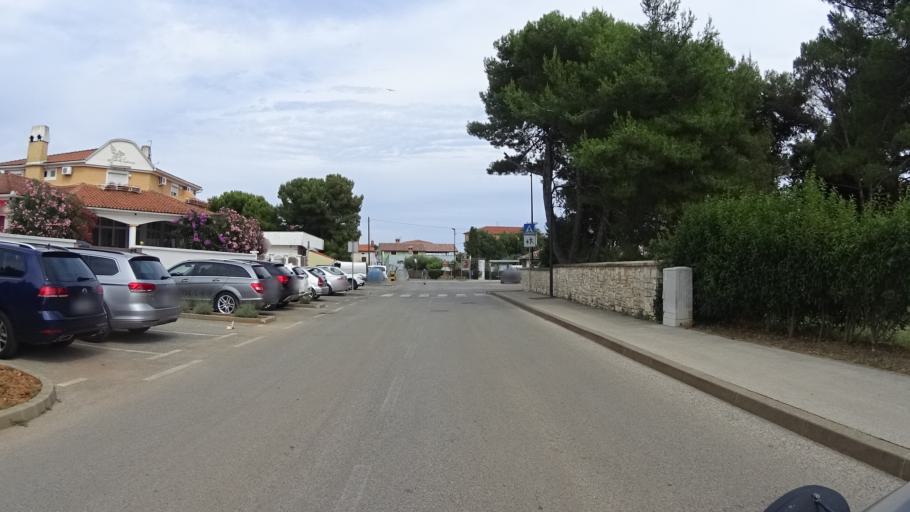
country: HR
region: Istarska
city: Medulin
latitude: 44.8245
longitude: 13.8952
